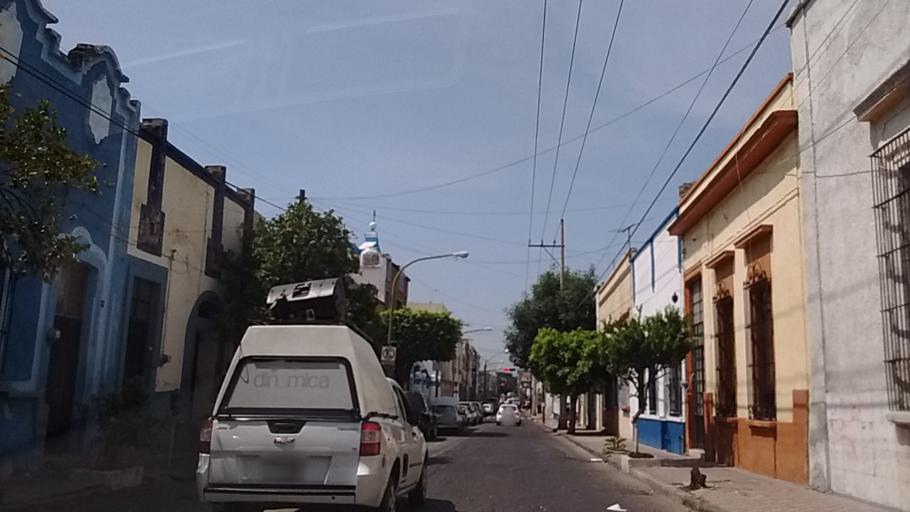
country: MX
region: Jalisco
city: Guadalajara
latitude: 20.6844
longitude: -103.3462
